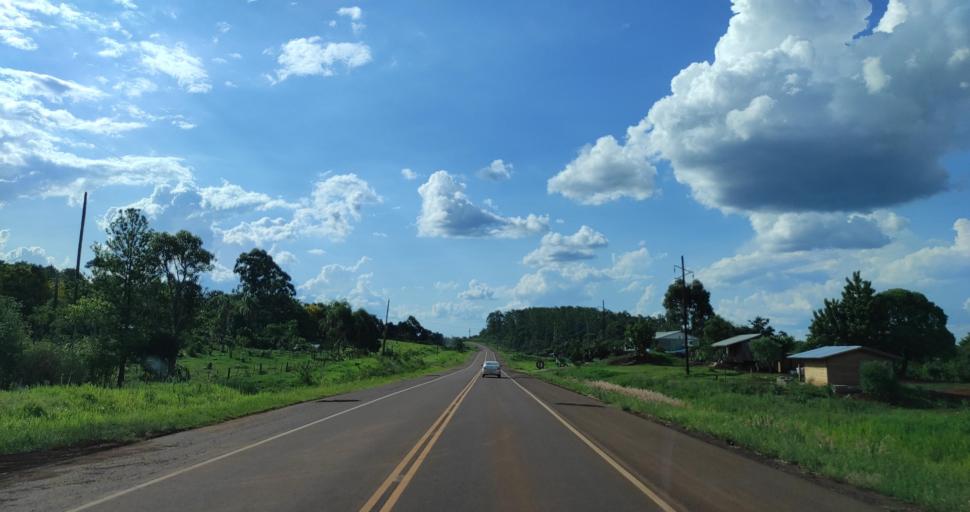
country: AR
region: Misiones
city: Bernardo de Irigoyen
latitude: -26.3841
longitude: -53.9142
